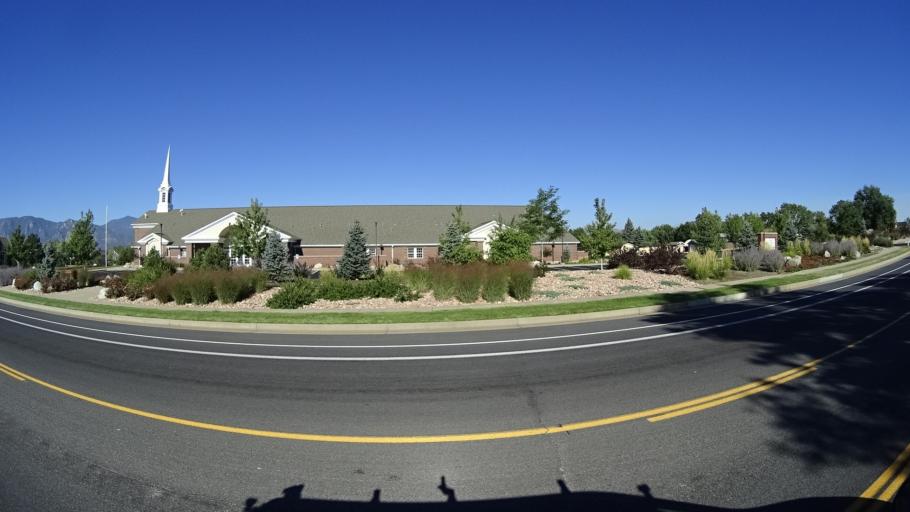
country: US
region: Colorado
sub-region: El Paso County
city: Cimarron Hills
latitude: 38.8130
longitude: -104.7326
